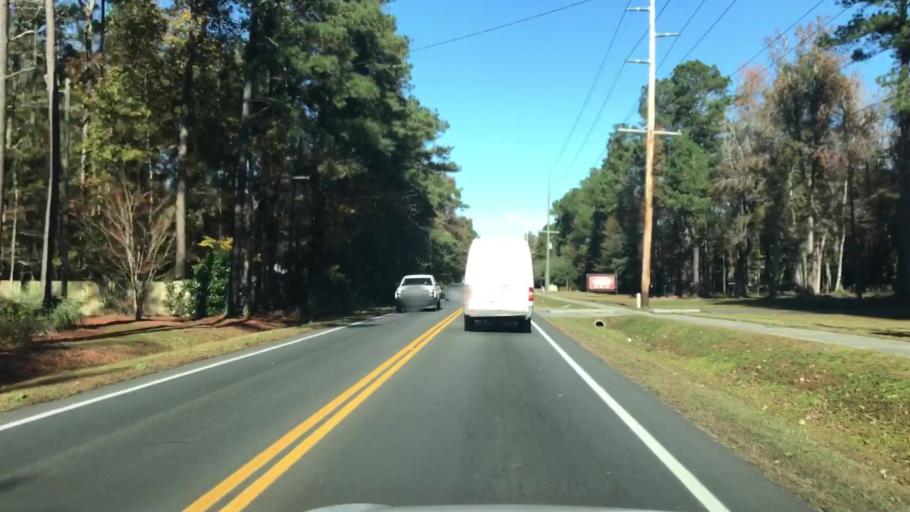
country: US
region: South Carolina
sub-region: Dorchester County
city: Summerville
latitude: 32.9999
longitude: -80.2307
